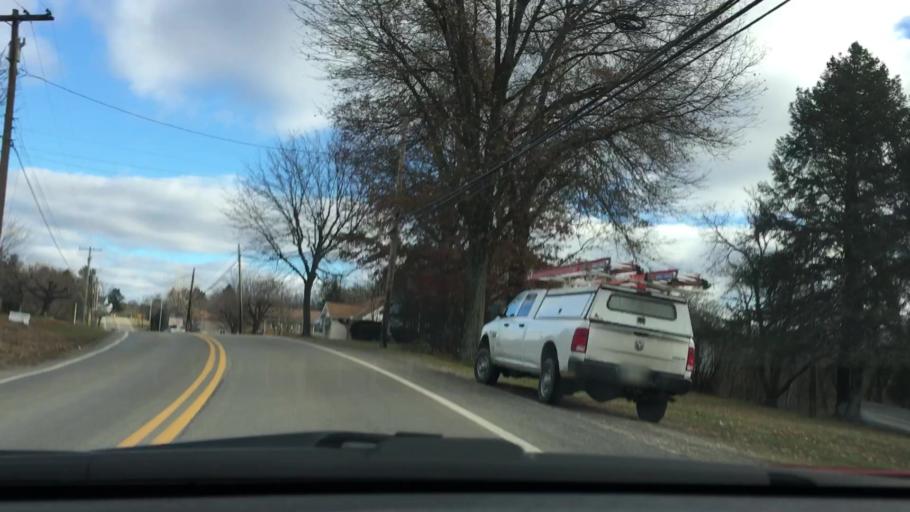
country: US
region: Pennsylvania
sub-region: Armstrong County
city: Orchard Hills
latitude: 40.5980
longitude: -79.5115
